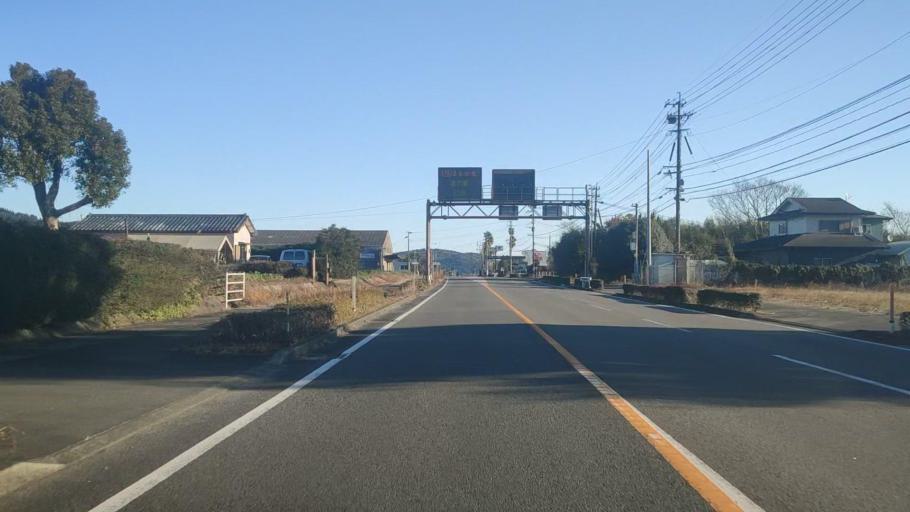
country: JP
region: Miyazaki
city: Takanabe
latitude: 32.3226
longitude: 131.5966
